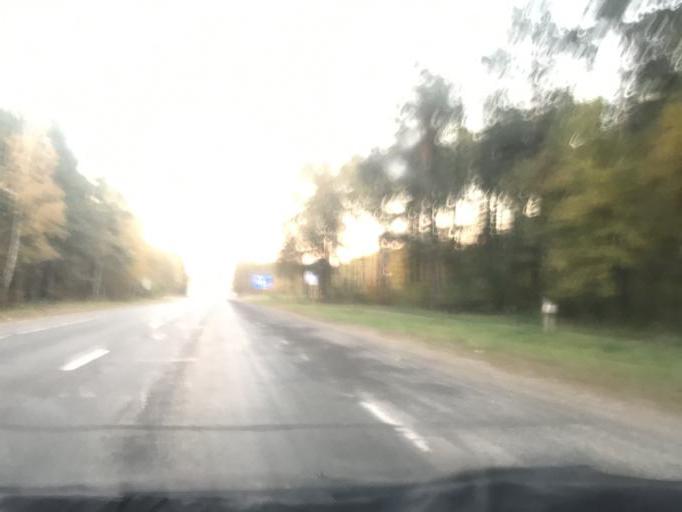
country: BY
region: Gomel
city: Kalinkavichy
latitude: 52.1260
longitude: 29.3634
